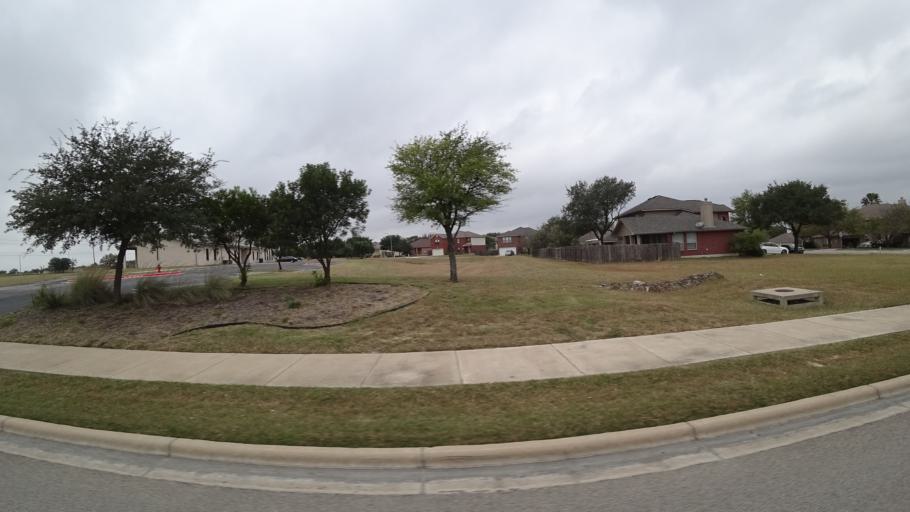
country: US
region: Texas
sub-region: Travis County
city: Windemere
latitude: 30.4682
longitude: -97.6292
